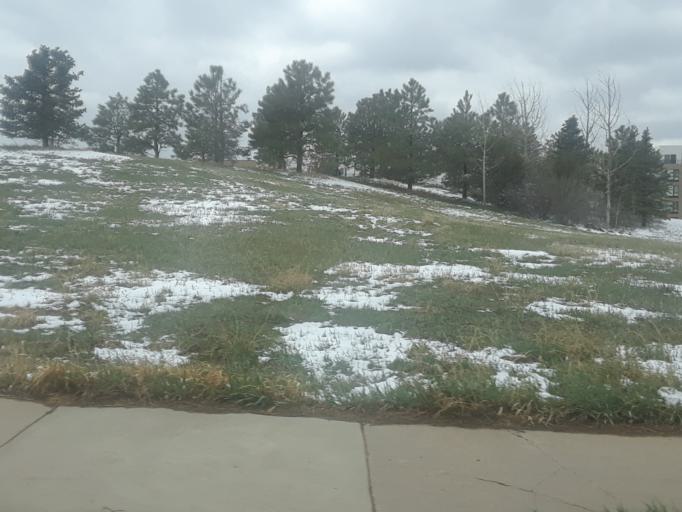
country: US
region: Colorado
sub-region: Arapahoe County
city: Centennial
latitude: 39.5741
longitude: -104.8764
